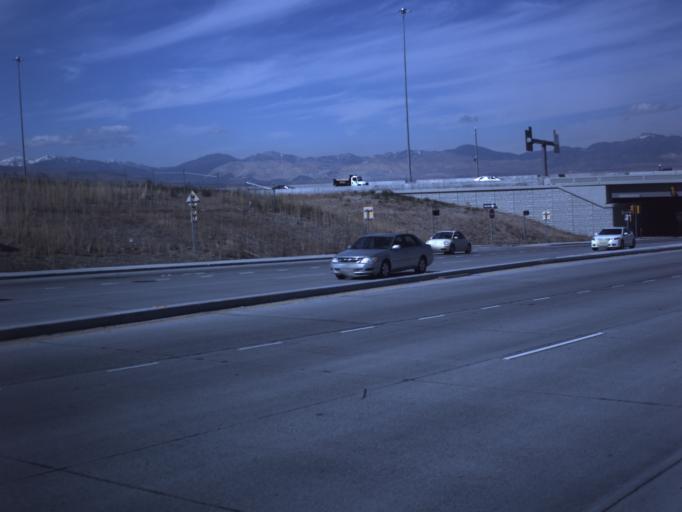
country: US
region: Utah
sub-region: Salt Lake County
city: Bluffdale
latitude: 40.4830
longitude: -111.8974
